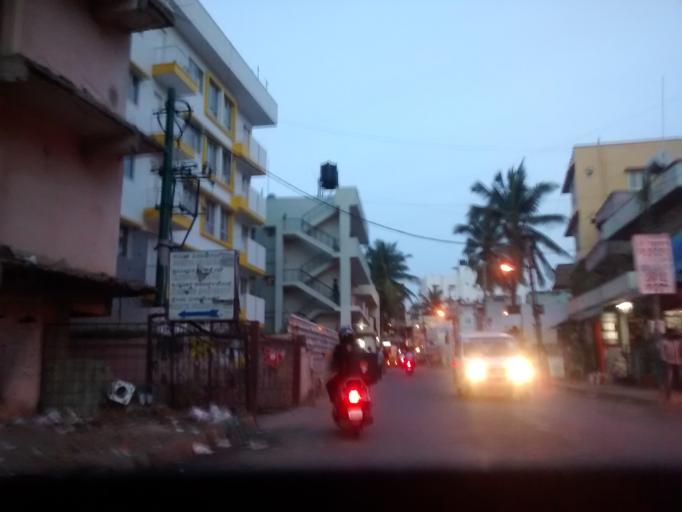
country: IN
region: Karnataka
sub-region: Bangalore Urban
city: Bangalore
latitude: 12.9750
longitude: 77.6650
